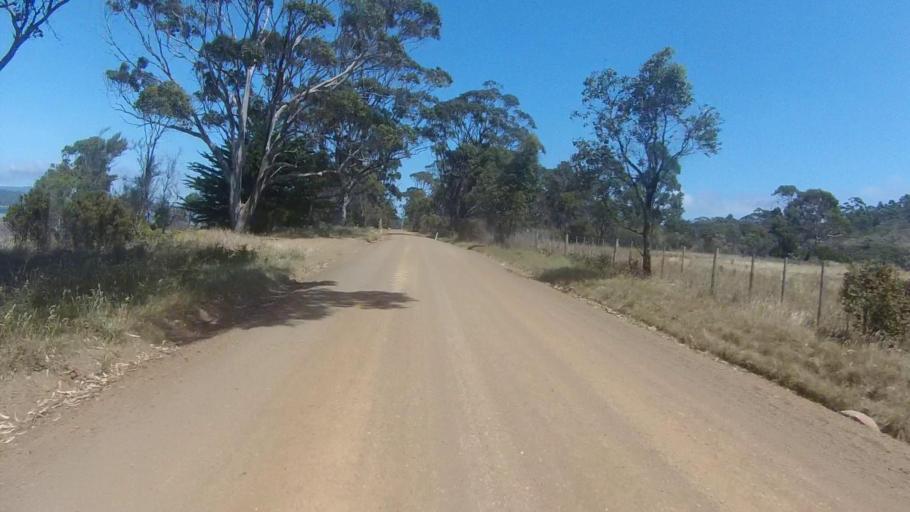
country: AU
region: Tasmania
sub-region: Sorell
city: Sorell
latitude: -42.8324
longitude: 147.8559
